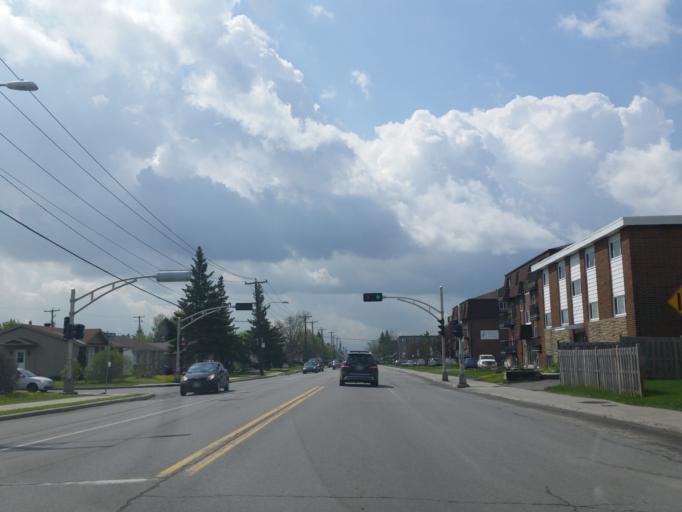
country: CA
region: Quebec
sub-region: Outaouais
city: Gatineau
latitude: 45.4867
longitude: -75.7025
